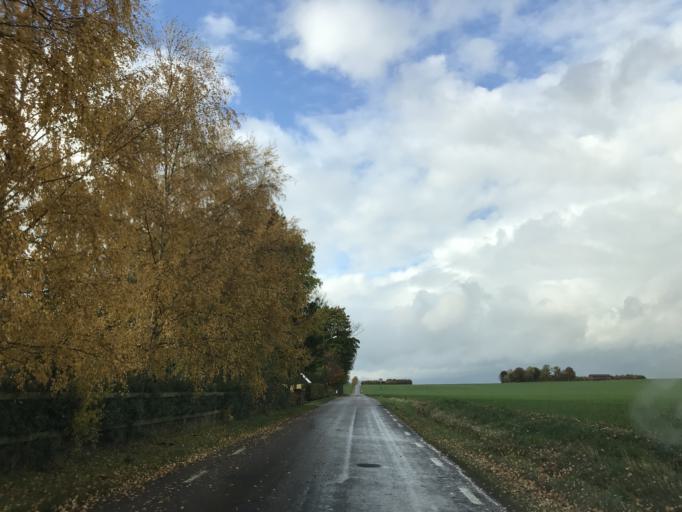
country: SE
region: Skane
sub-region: Svalovs Kommun
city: Svaloev
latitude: 55.9035
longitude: 13.1796
